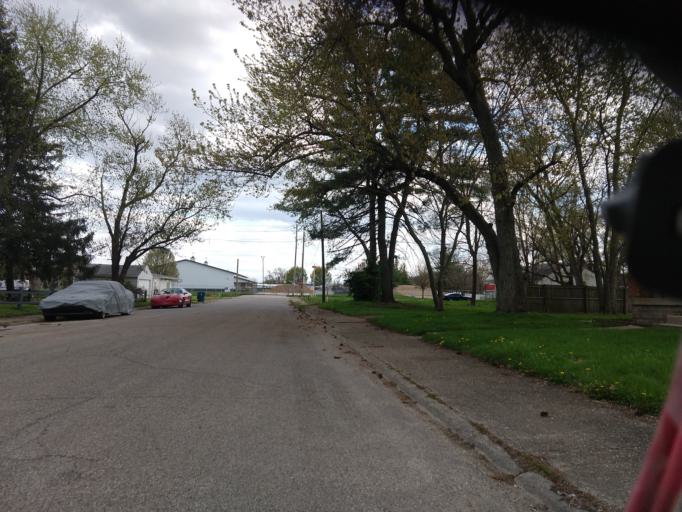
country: US
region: Indiana
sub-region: Marion County
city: Broad Ripple
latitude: 39.8337
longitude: -86.1289
